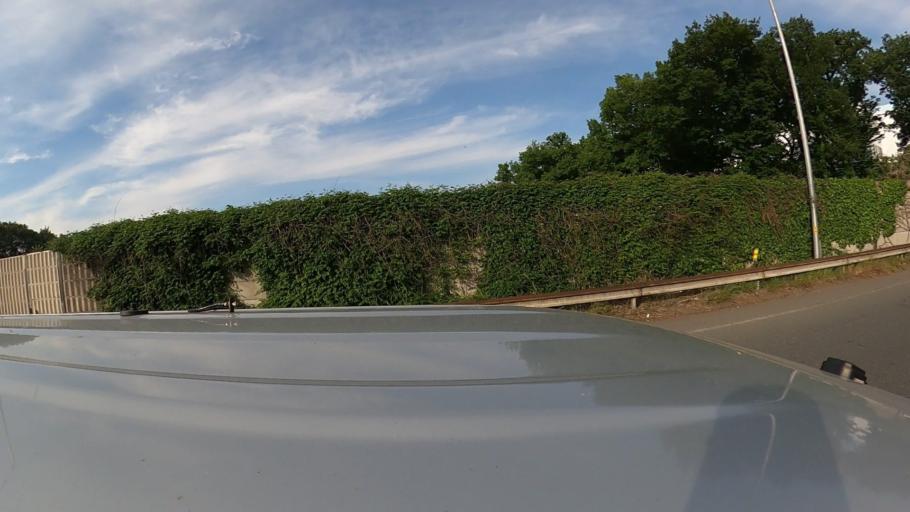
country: JP
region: Saitama
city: Oi
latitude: 35.8066
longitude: 139.5321
